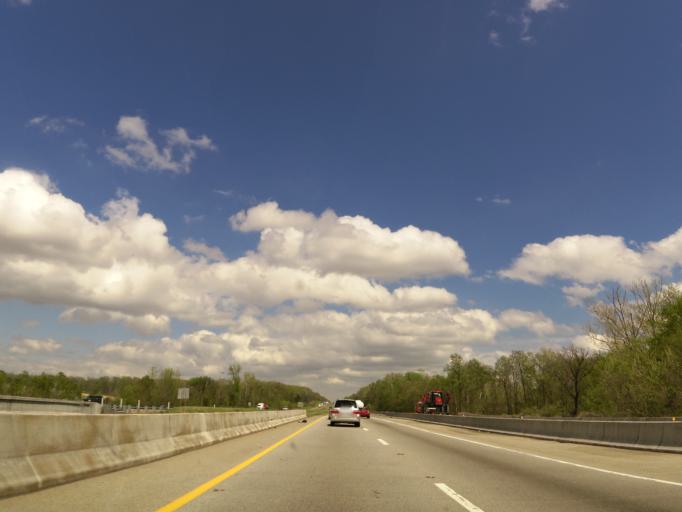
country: US
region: Tennessee
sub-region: Shelby County
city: Arlington
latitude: 35.2637
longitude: -89.6620
